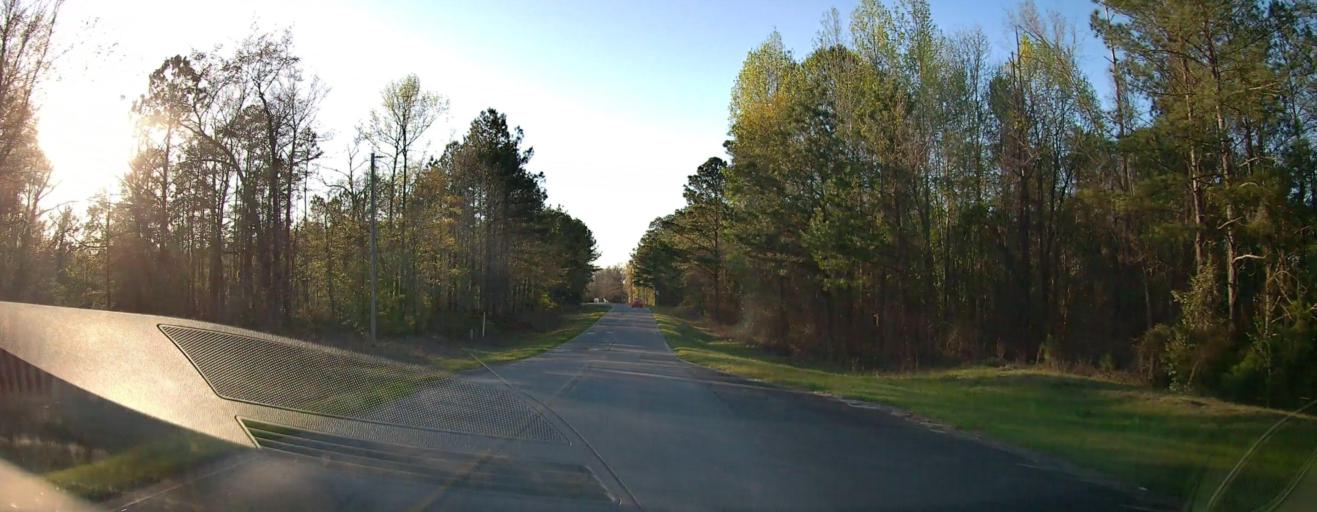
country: US
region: Georgia
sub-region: Wilkinson County
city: Gordon
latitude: 32.8750
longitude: -83.2492
